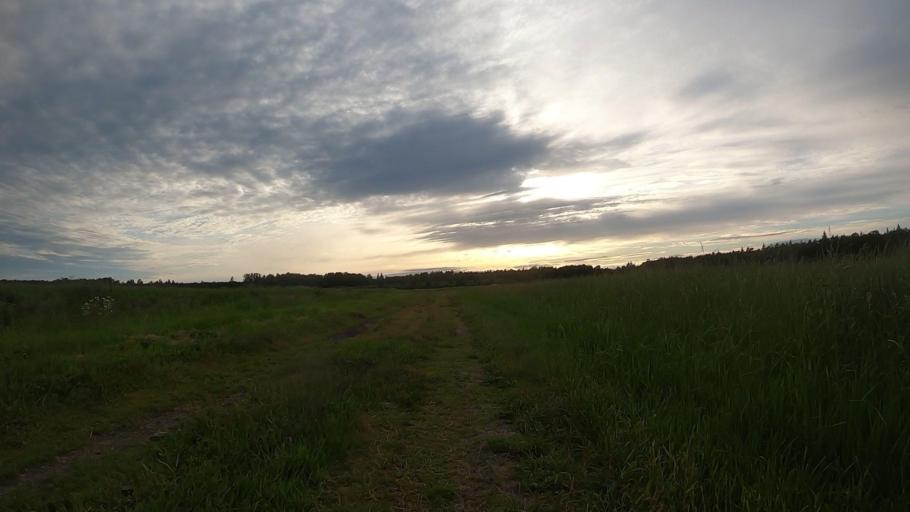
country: LV
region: Olaine
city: Olaine
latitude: 56.8245
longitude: 23.9500
